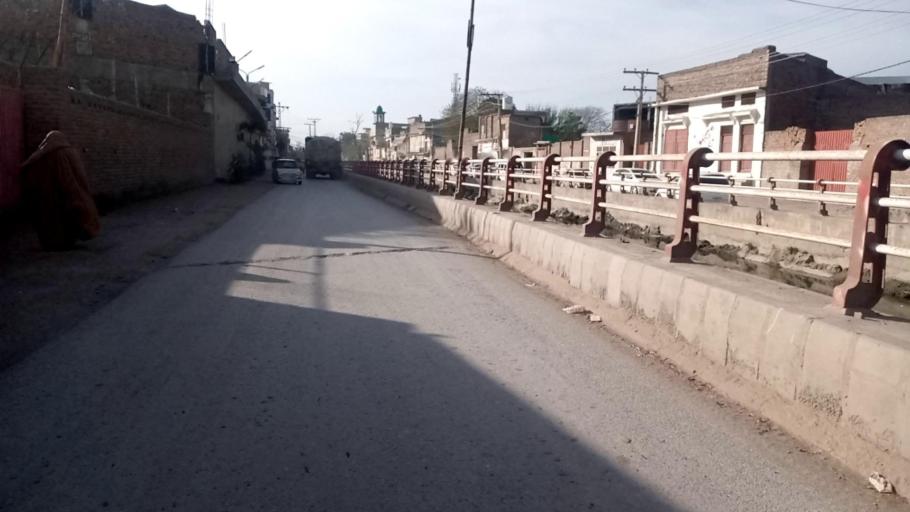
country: PK
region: Khyber Pakhtunkhwa
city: Peshawar
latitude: 34.0098
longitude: 71.6184
